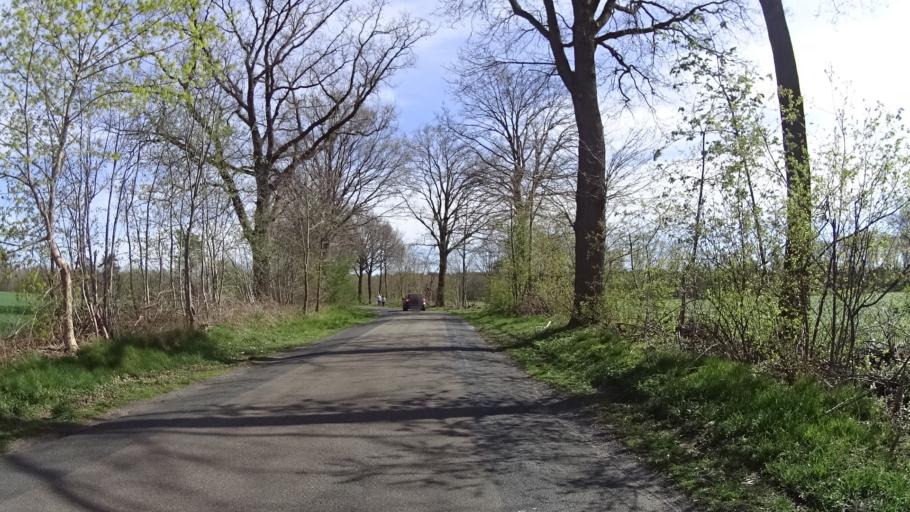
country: DE
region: North Rhine-Westphalia
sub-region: Regierungsbezirk Munster
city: Dreierwalde
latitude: 52.2724
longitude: 7.4830
